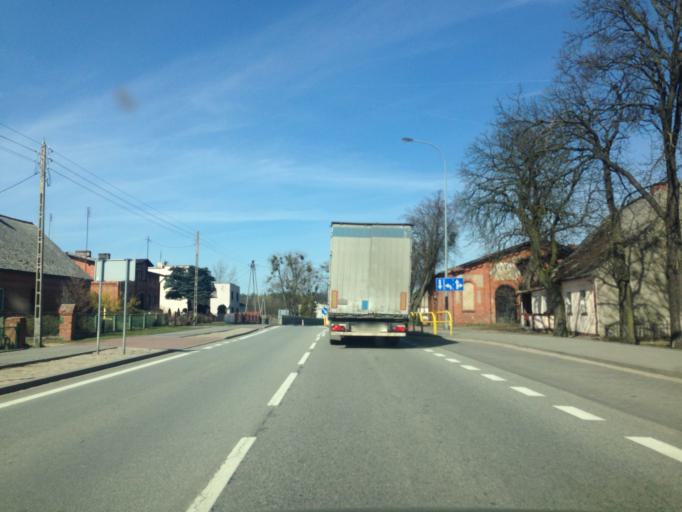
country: PL
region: Pomeranian Voivodeship
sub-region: Powiat starogardzki
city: Smetowo Graniczne
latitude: 53.7315
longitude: 18.7342
